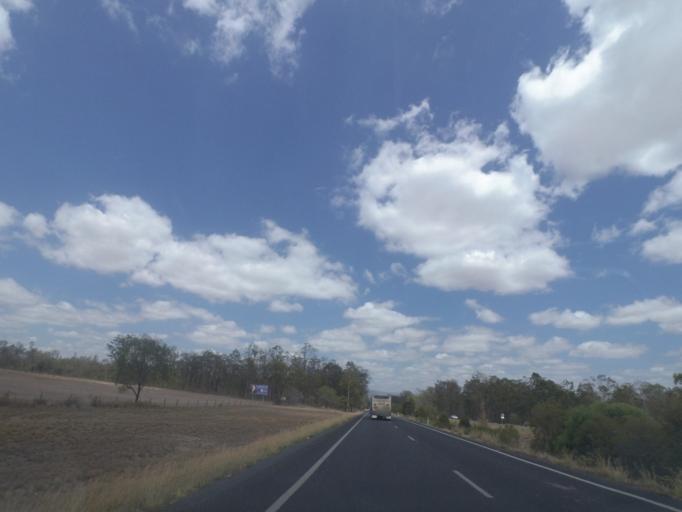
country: AU
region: Queensland
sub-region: Lockyer Valley
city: Gatton
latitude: -27.5520
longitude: 152.1517
